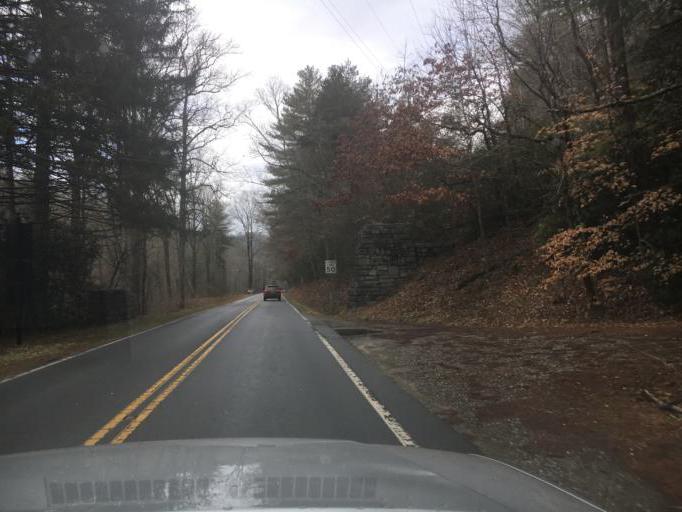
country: US
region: North Carolina
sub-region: Transylvania County
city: Brevard
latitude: 35.2745
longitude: -82.7068
